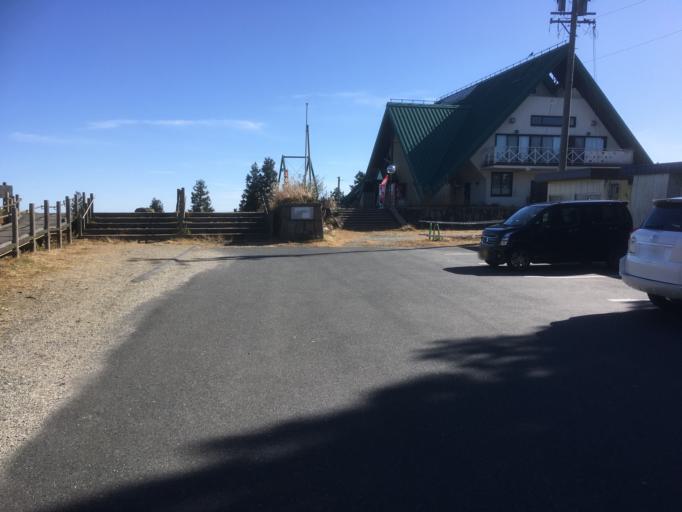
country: JP
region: Mie
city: Ueno-ebisumachi
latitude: 34.6885
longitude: 136.2756
